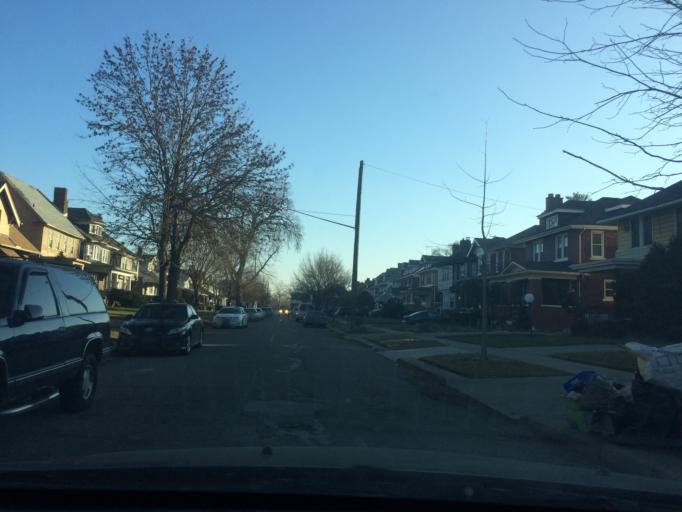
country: US
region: Michigan
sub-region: Wayne County
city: Highland Park
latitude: 42.3669
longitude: -83.0890
